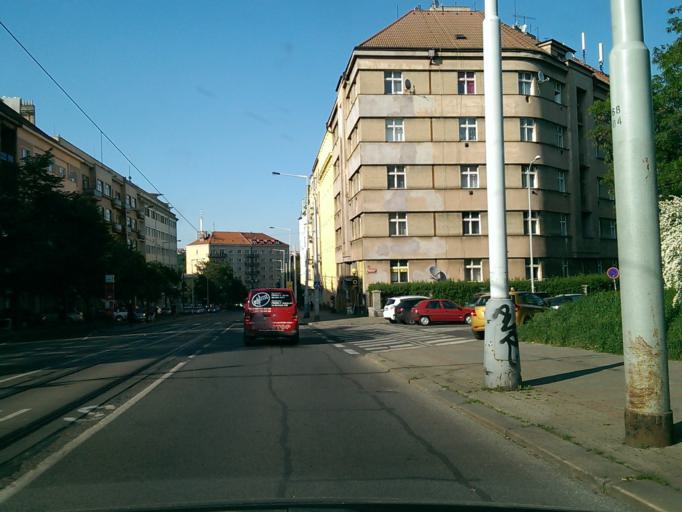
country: CZ
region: Praha
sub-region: Praha 2
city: Vysehrad
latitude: 50.0608
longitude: 14.4367
